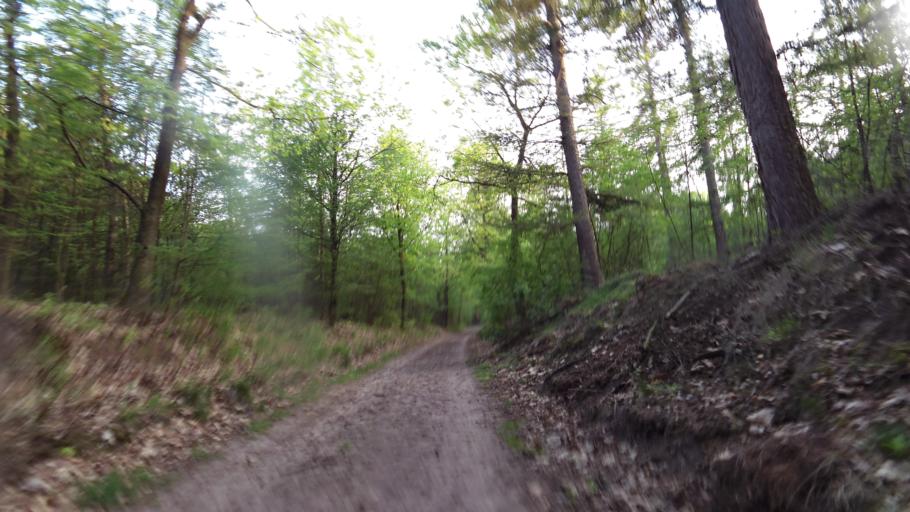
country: NL
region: Gelderland
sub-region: Gemeente Ede
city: Ede
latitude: 52.0595
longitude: 5.6771
